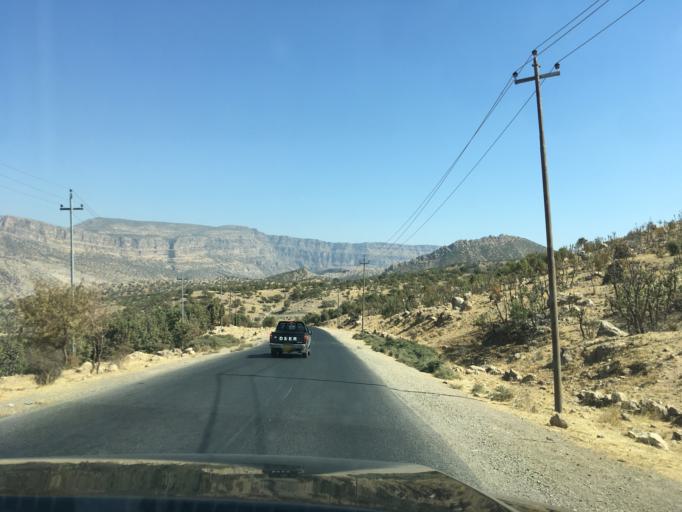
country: IQ
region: Arbil
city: Ruwandiz
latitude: 36.6488
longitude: 44.3500
